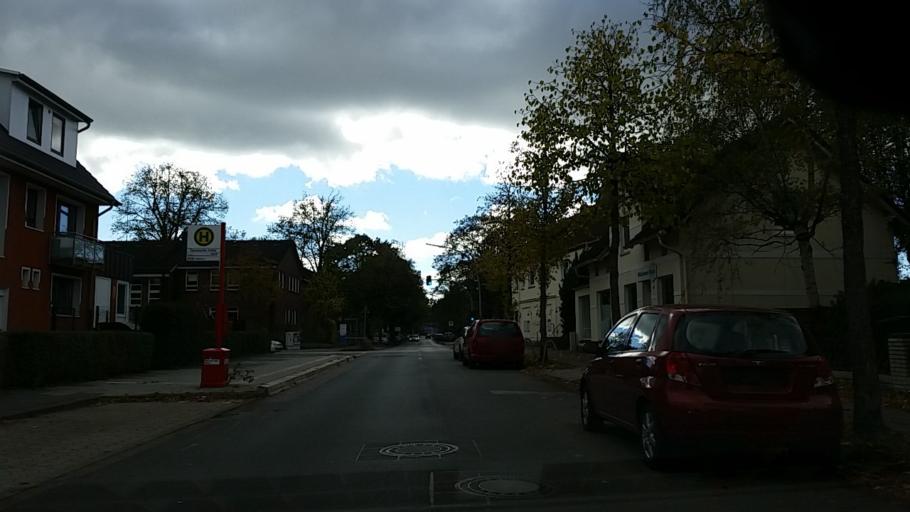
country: DE
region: Hamburg
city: Wandsbek
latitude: 53.5426
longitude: 10.1276
